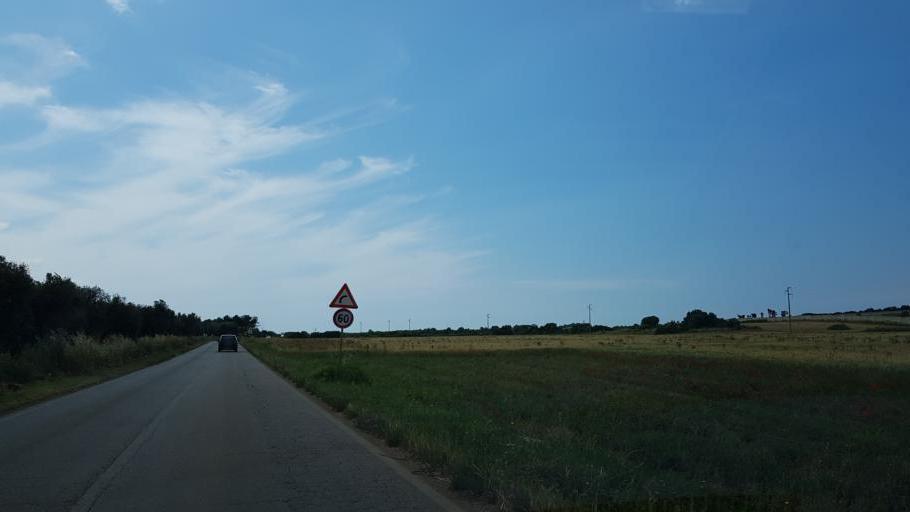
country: IT
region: Apulia
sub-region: Provincia di Lecce
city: Porto Cesareo
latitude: 40.3312
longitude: 17.8521
